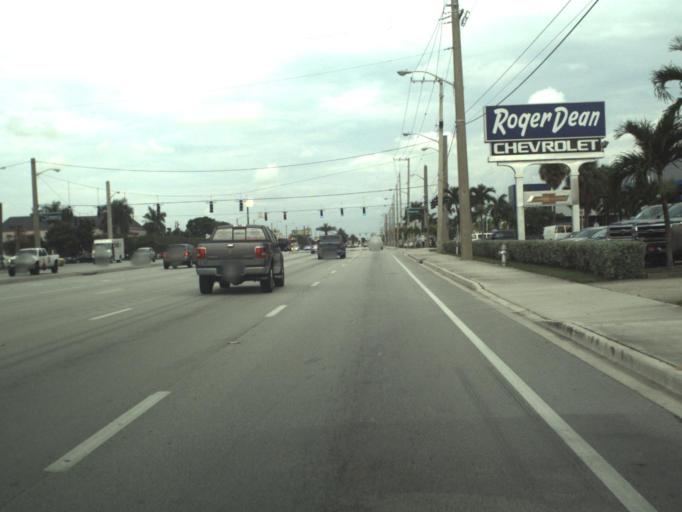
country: US
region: Florida
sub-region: Palm Beach County
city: Schall Circle
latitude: 26.7065
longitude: -80.0852
